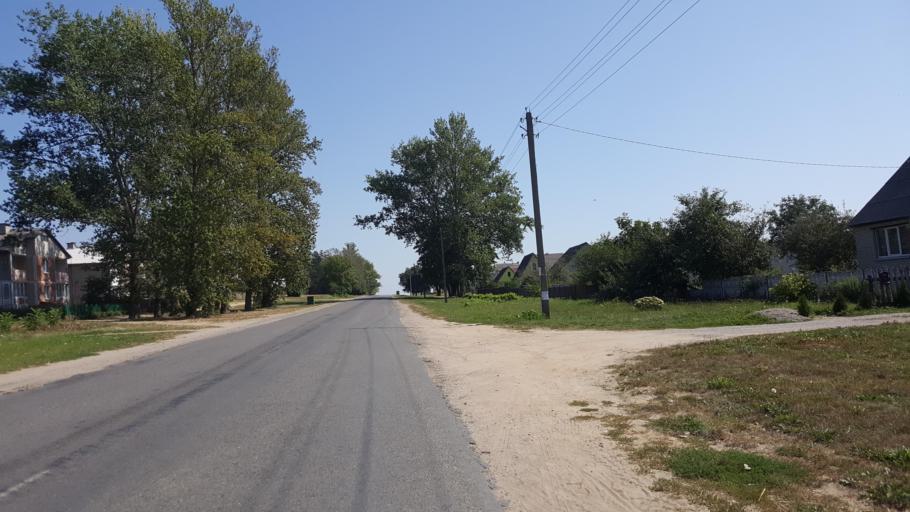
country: BY
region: Brest
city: Vysokaye
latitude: 52.4410
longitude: 23.4638
